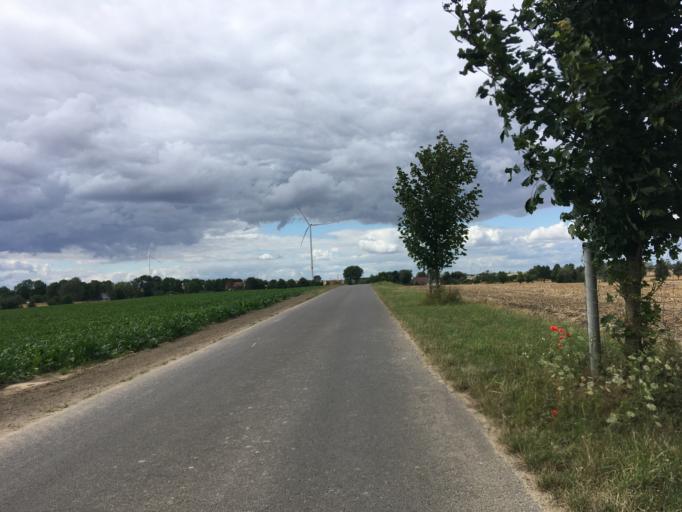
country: DE
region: Brandenburg
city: Gramzow
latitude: 53.2669
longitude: 14.0145
